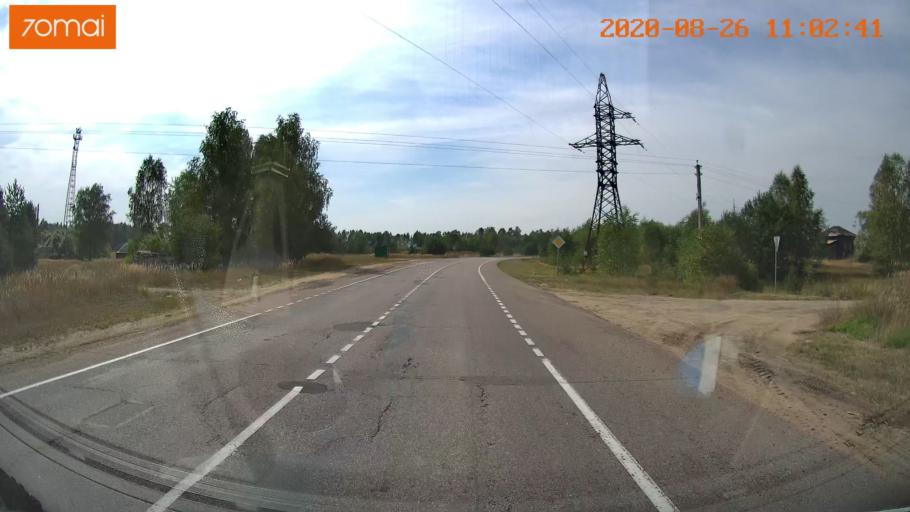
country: RU
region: Rjazan
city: Izhevskoye
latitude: 54.5475
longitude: 41.2229
